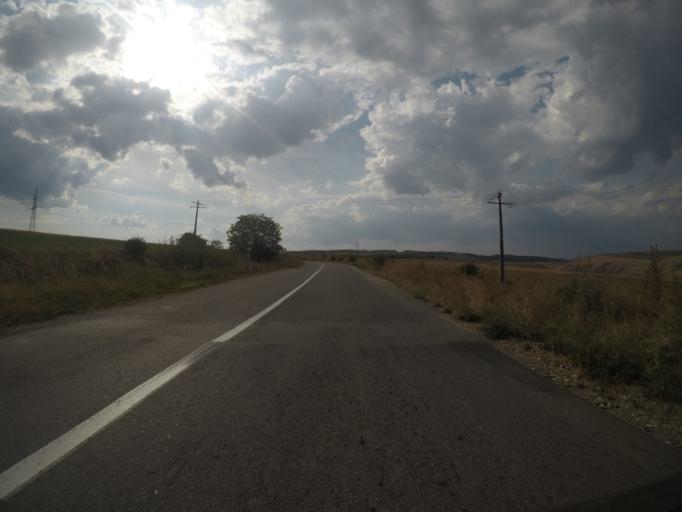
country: RO
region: Cluj
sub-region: Comuna Sandulesti
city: Copaceni
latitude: 46.5864
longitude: 23.7376
